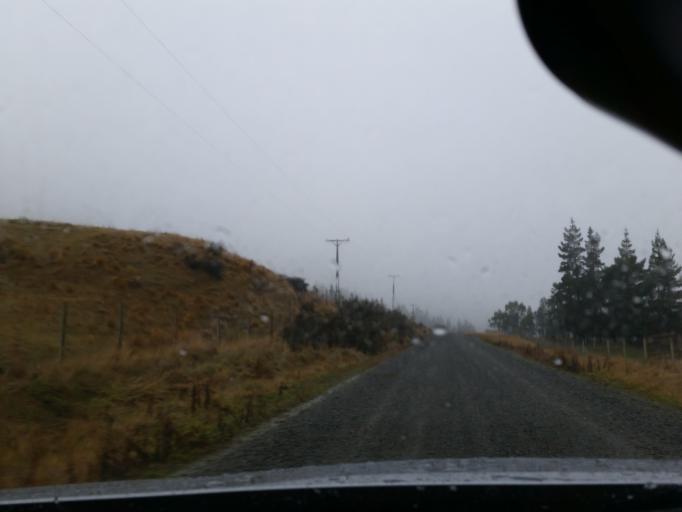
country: NZ
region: Southland
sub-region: Southland District
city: Te Anau
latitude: -45.5882
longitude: 168.0667
